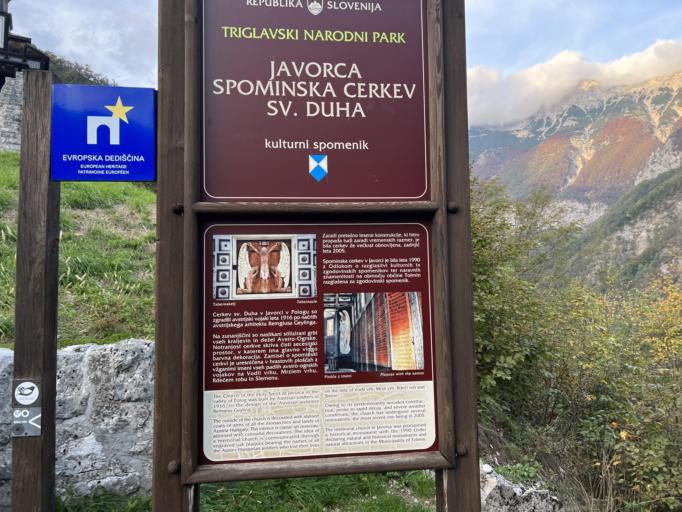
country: SI
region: Tolmin
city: Tolmin
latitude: 46.2344
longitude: 13.7200
